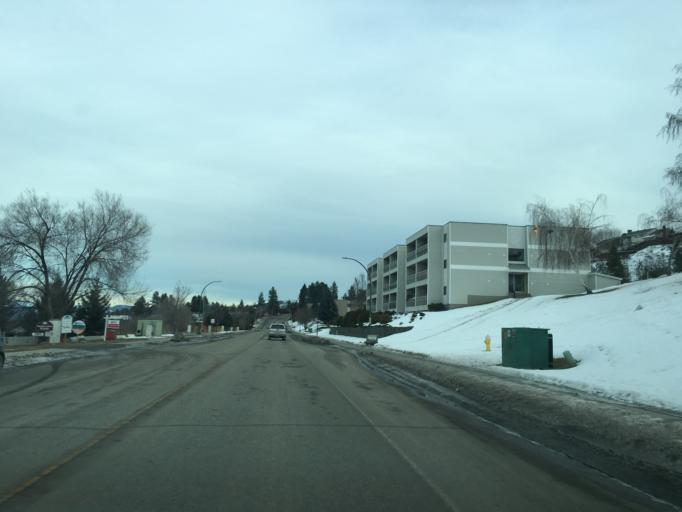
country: CA
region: British Columbia
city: Kamloops
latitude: 50.6488
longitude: -120.3681
